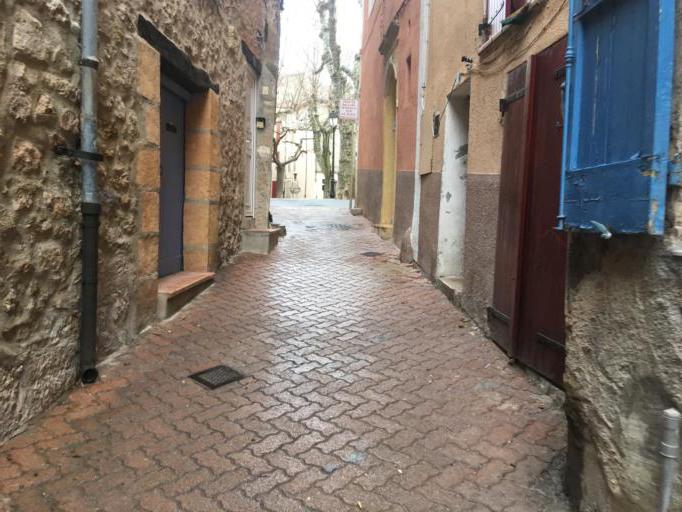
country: FR
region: Provence-Alpes-Cote d'Azur
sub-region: Departement du Var
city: Rians
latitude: 43.6070
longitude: 5.7557
